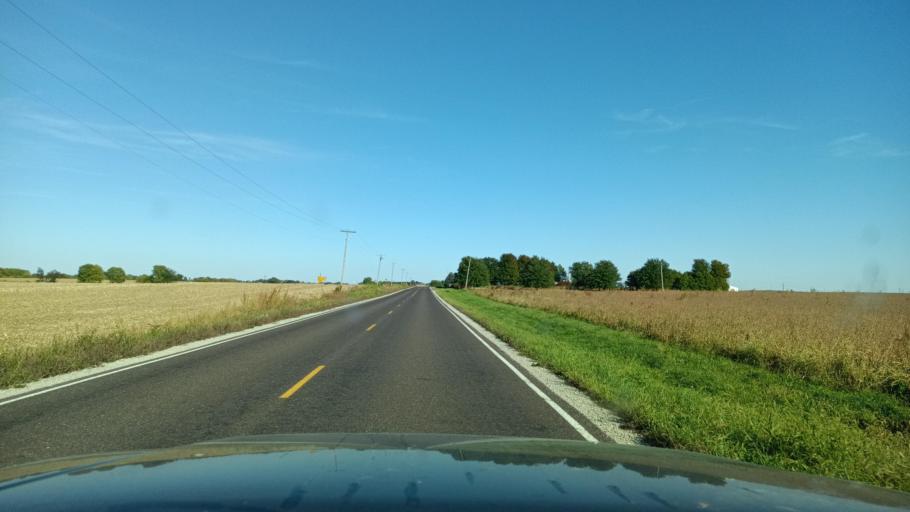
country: US
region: Illinois
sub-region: Logan County
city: Atlanta
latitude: 40.2386
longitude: -89.1122
